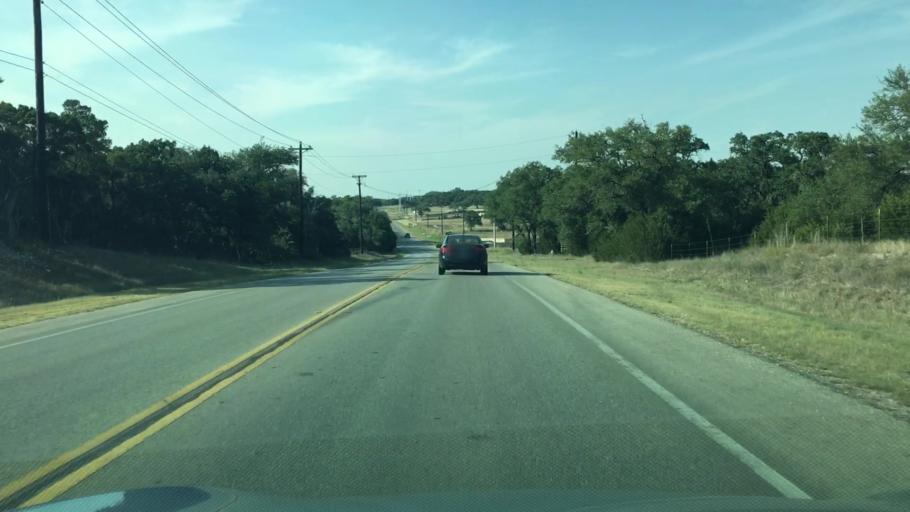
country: US
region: Texas
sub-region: Hays County
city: Dripping Springs
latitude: 30.1601
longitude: -98.0087
